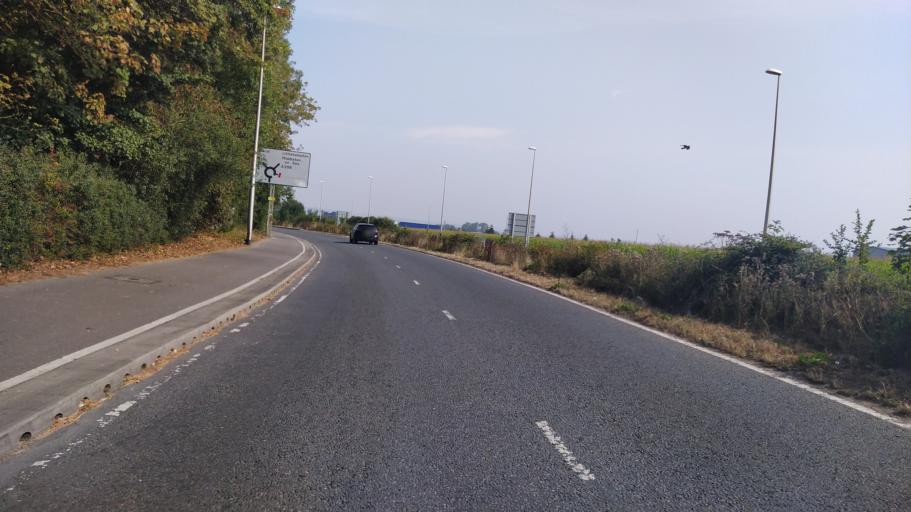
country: GB
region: England
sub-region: West Sussex
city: Bognor Regis
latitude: 50.8045
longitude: -0.6666
